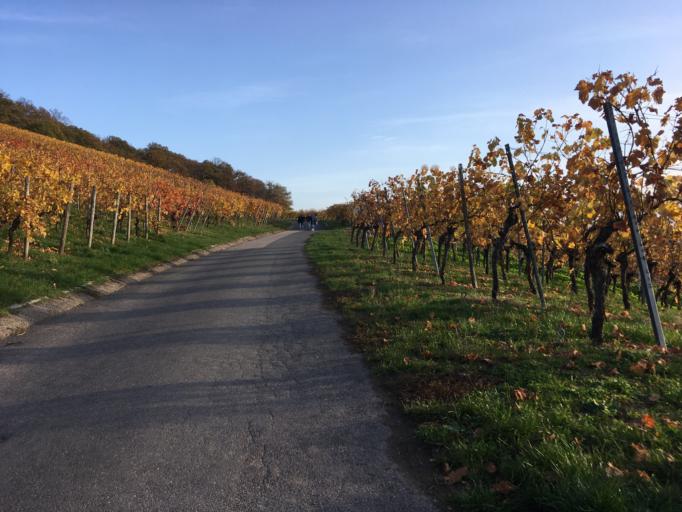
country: DE
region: Baden-Wuerttemberg
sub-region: Regierungsbezirk Stuttgart
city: Erlenbach
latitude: 49.1490
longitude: 9.2522
